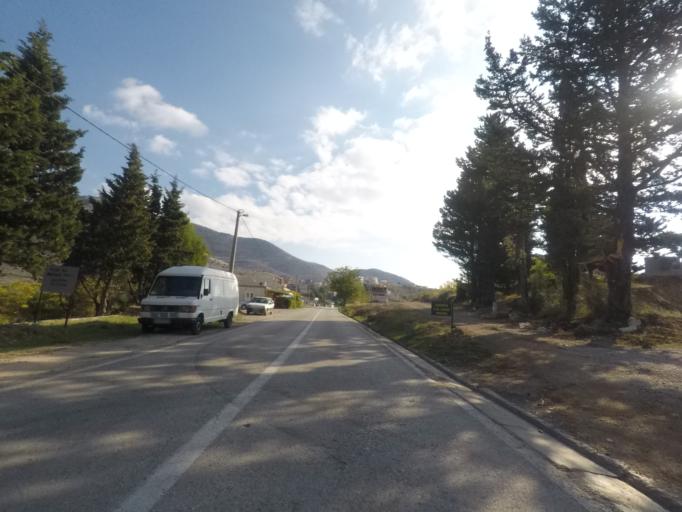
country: HR
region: Dubrovacko-Neretvanska
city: Cibaca
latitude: 42.6593
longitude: 18.1653
